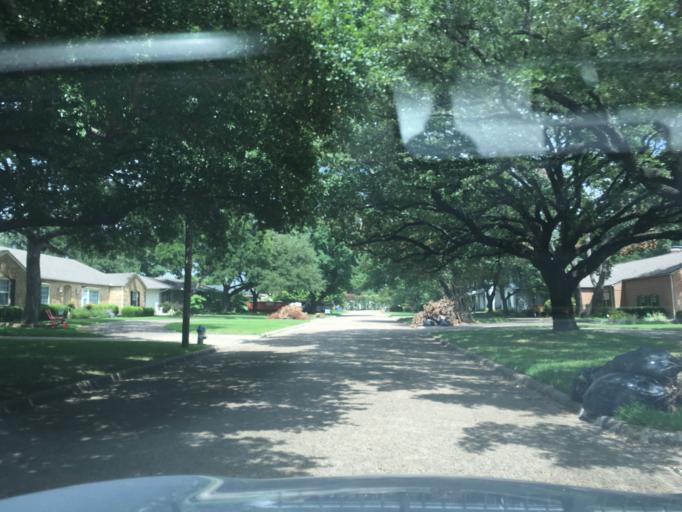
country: US
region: Texas
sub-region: Dallas County
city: Addison
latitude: 32.9073
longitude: -96.8179
